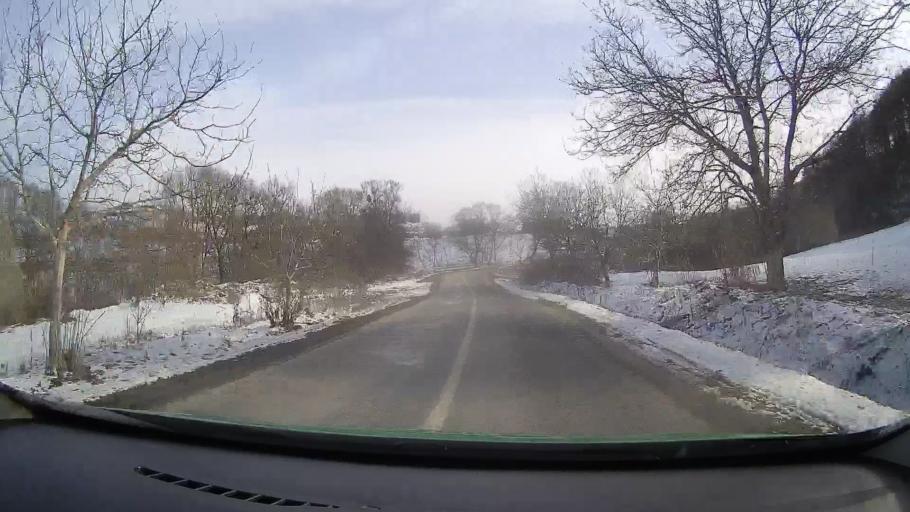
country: RO
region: Mures
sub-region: Comuna Apold
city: Saes
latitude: 46.1651
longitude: 24.7578
